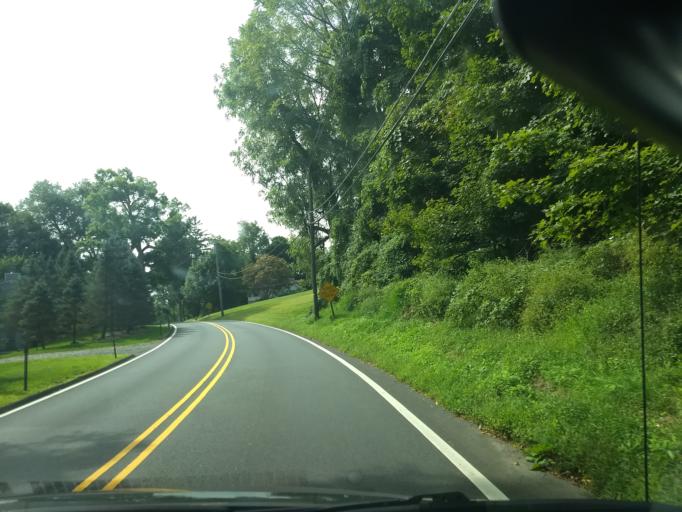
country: US
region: New Jersey
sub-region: Morris County
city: Morris Plains
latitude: 40.8226
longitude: -74.4938
